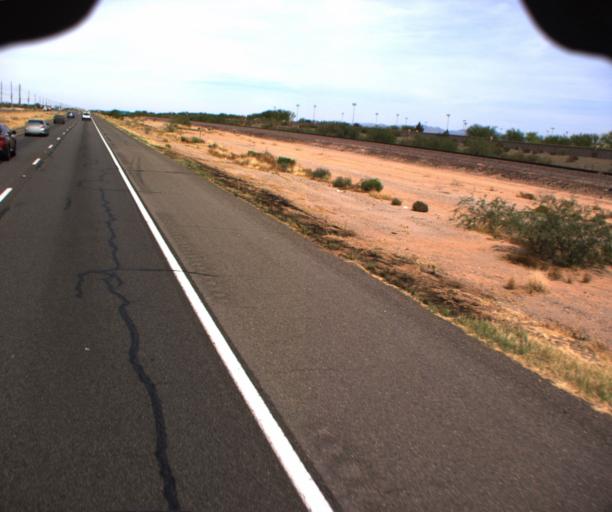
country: US
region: Arizona
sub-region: Maricopa County
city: Sun City West
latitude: 33.6921
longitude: -112.4185
